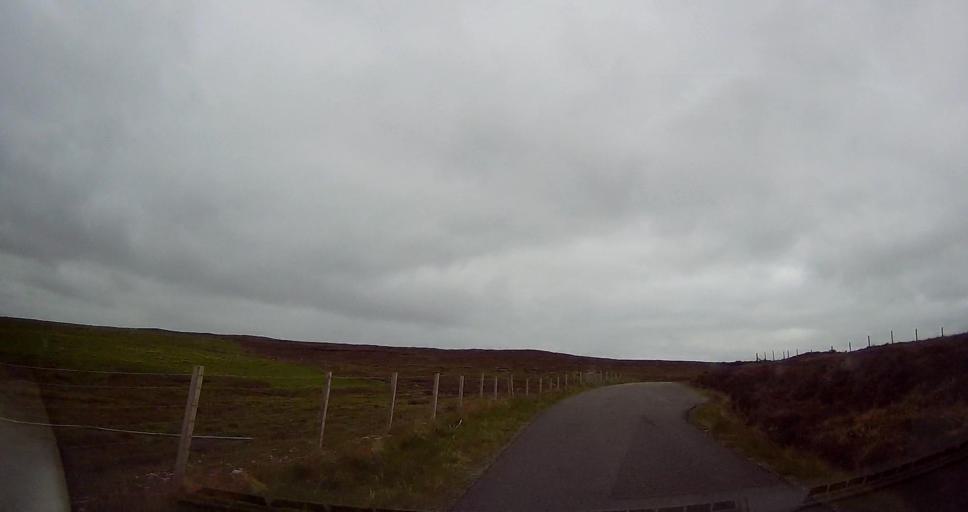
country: GB
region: Scotland
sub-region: Shetland Islands
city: Lerwick
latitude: 60.3103
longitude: -1.3376
